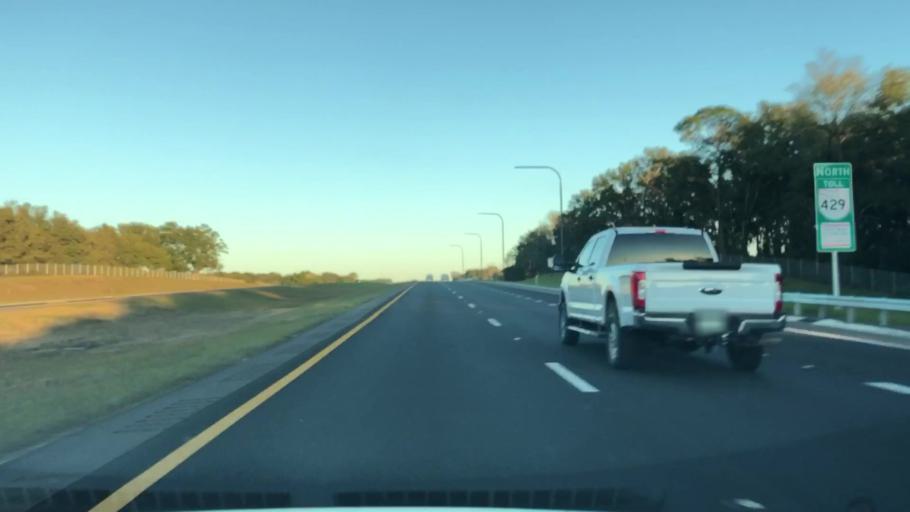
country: US
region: Florida
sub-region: Lake County
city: Mount Plymouth
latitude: 28.7756
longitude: -81.5489
